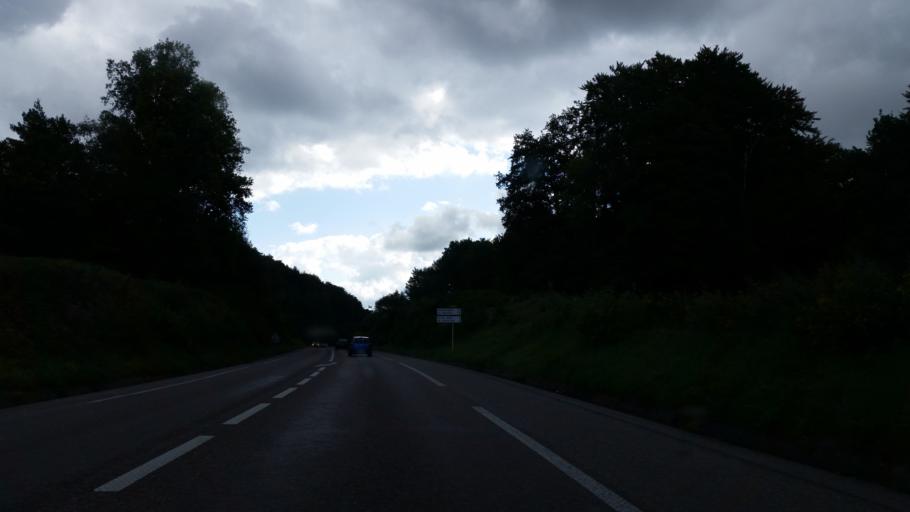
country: FR
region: Lorraine
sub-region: Departement des Vosges
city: Saint-Etienne-les-Remiremont
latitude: 48.0159
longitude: 6.6186
